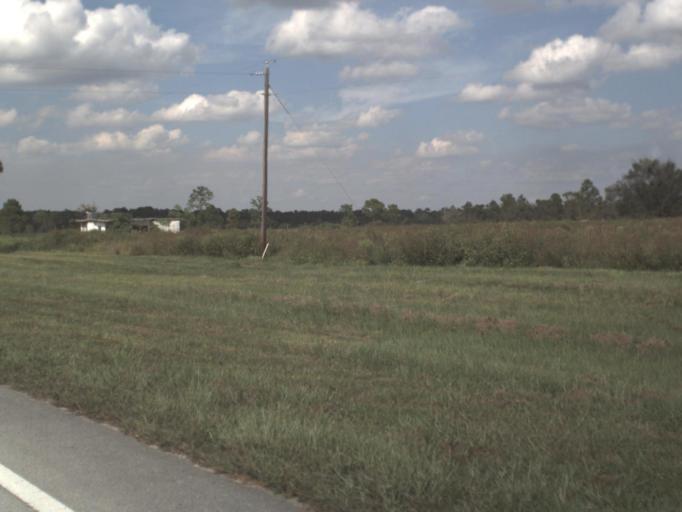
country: US
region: Florida
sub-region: Indian River County
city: Fellsmere
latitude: 27.6412
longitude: -80.8742
